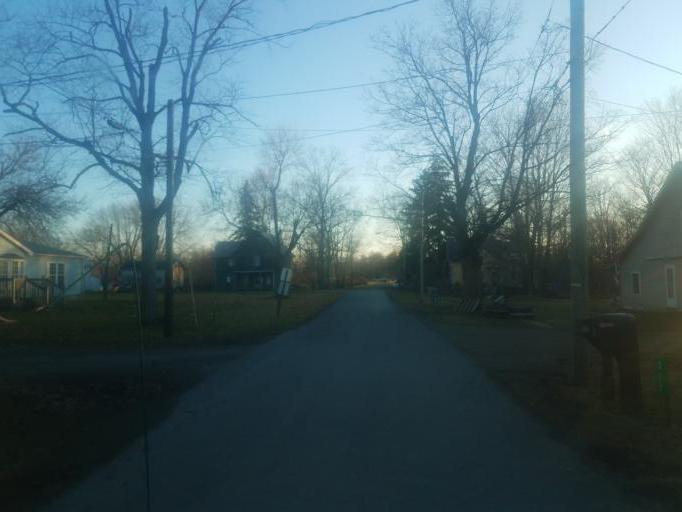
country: US
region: Ohio
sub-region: Wyandot County
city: Upper Sandusky
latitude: 40.8197
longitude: -83.1338
